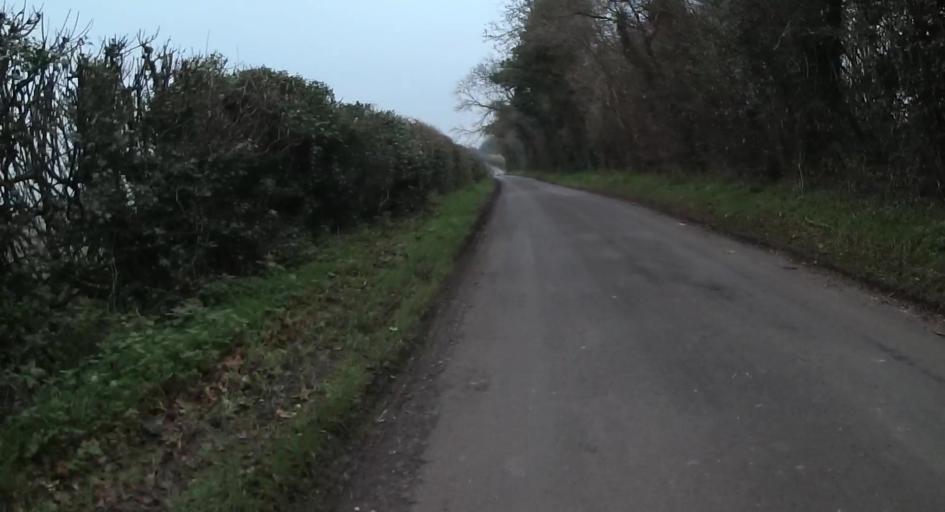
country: GB
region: England
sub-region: Hampshire
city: Kings Worthy
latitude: 51.1161
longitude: -1.2112
